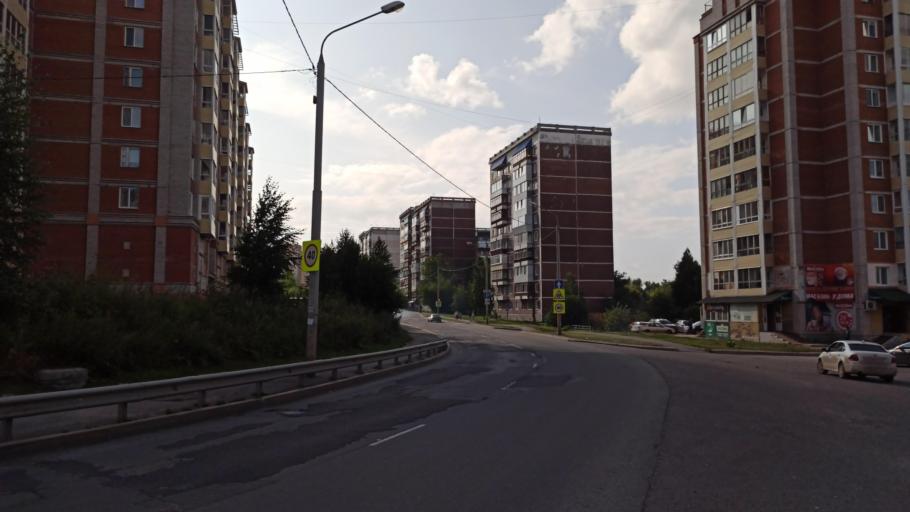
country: RU
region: Tomsk
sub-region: Tomskiy Rayon
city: Tomsk
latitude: 56.4824
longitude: 85.0138
